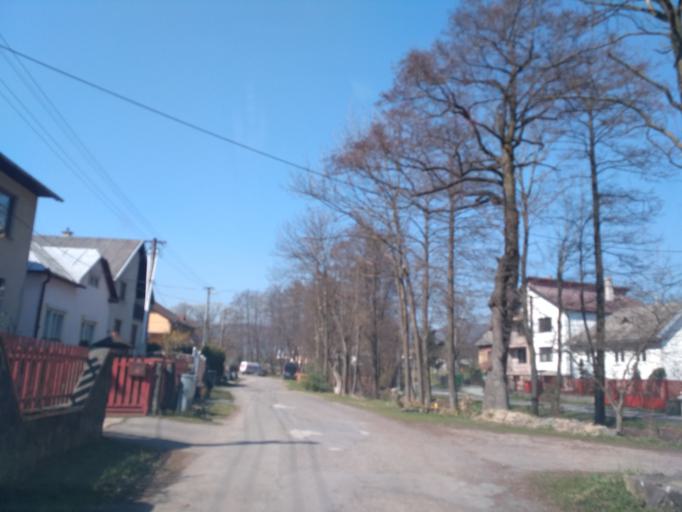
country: SK
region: Presovsky
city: Vranov nad Topl'ou
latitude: 48.8265
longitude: 21.6265
